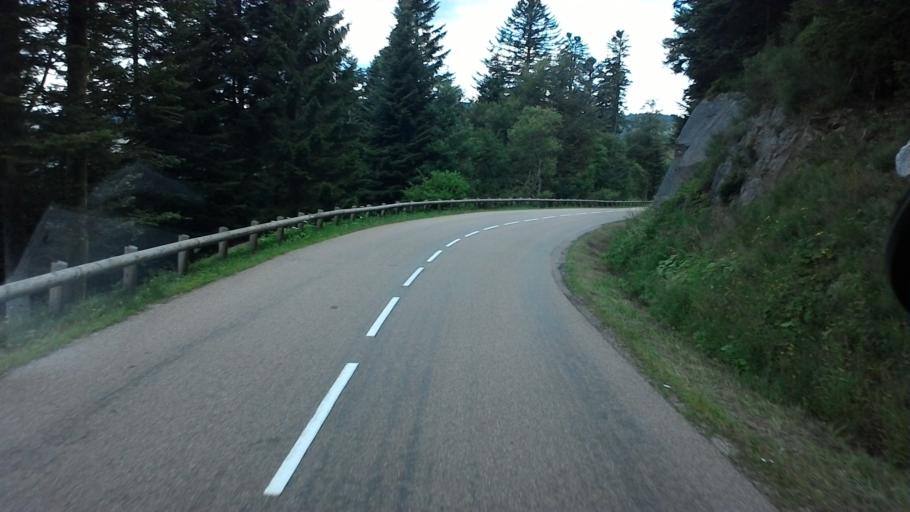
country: FR
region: Lorraine
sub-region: Departement des Vosges
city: La Bresse
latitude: 48.0318
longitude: 6.8668
